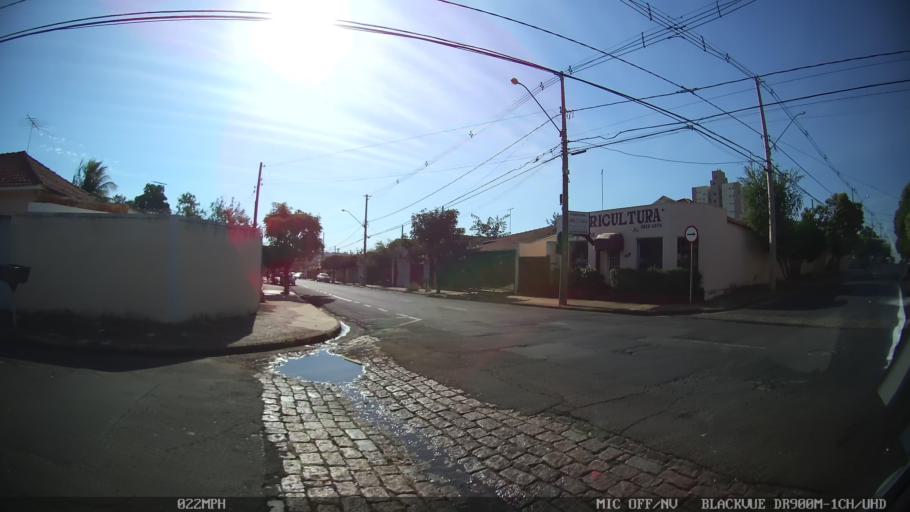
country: BR
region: Sao Paulo
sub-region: Sao Jose Do Rio Preto
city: Sao Jose do Rio Preto
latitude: -20.7980
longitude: -49.3908
